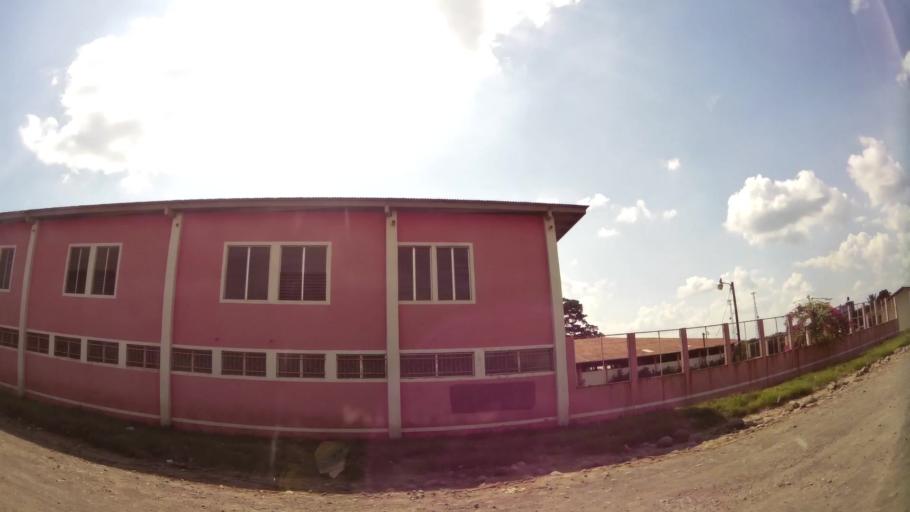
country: GT
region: Suchitepeque
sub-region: Municipio de Cuyotenango
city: Cuyotenango
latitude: 14.5440
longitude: -91.5684
